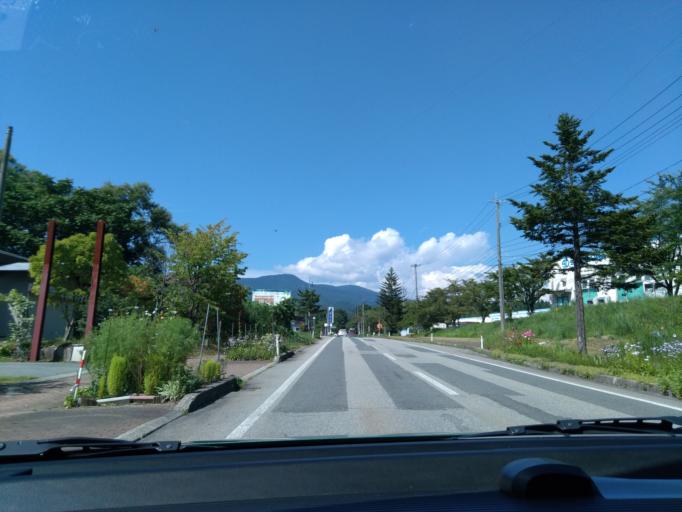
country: JP
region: Akita
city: Kakunodatemachi
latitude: 39.7433
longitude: 140.7200
